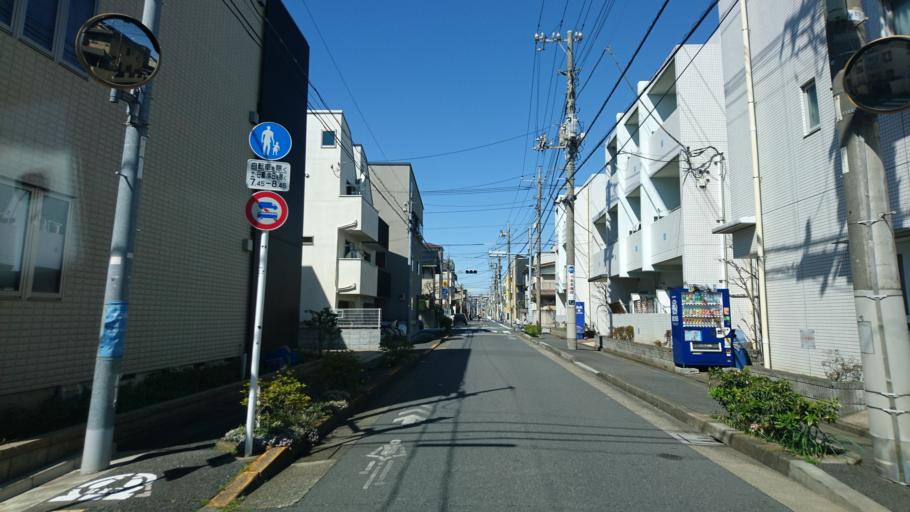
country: JP
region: Kanagawa
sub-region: Kawasaki-shi
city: Kawasaki
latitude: 35.5681
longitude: 139.7009
